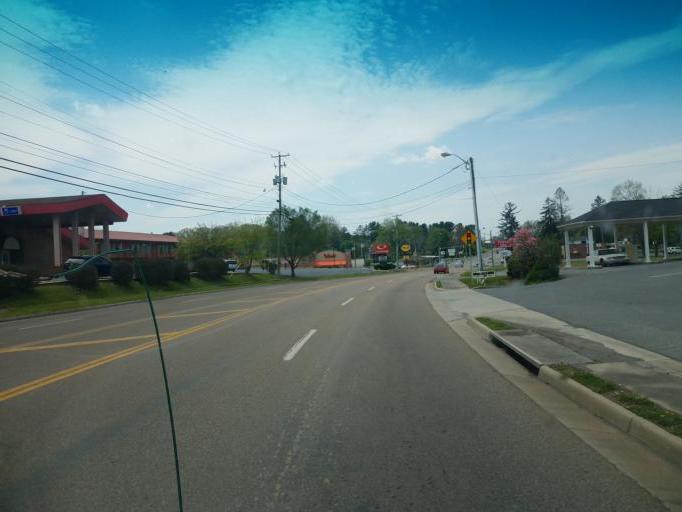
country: US
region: Virginia
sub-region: Smyth County
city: Marion
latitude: 36.8462
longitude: -81.4930
